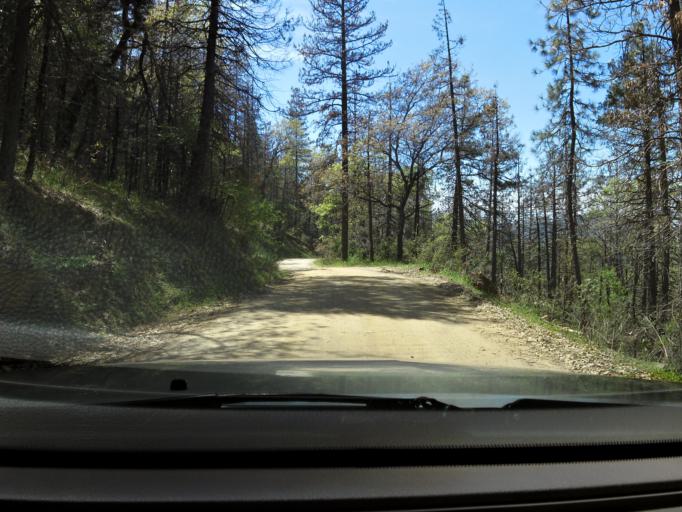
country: US
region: California
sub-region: Madera County
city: Oakhurst
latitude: 37.2837
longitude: -119.5869
